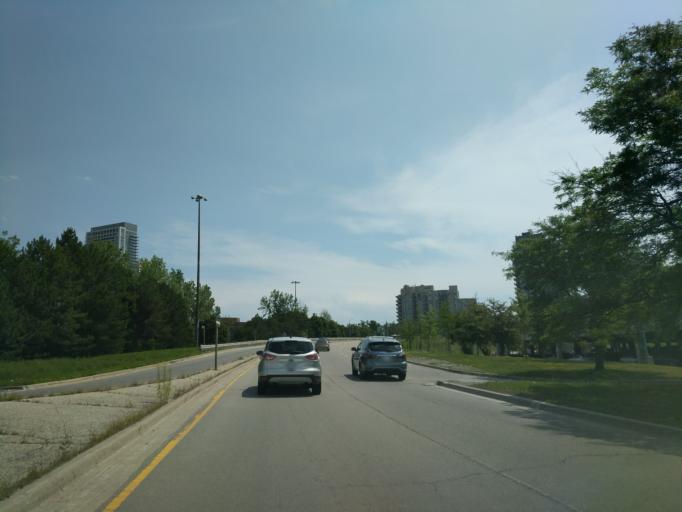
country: CA
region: Ontario
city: Willowdale
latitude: 43.7786
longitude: -79.3415
